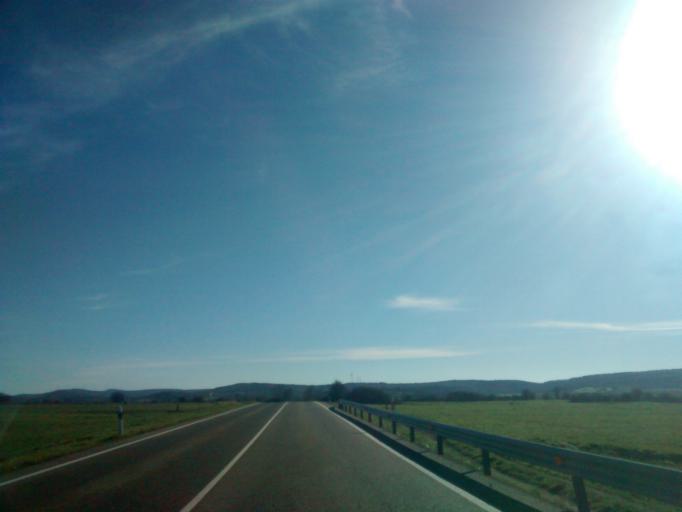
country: ES
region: Cantabria
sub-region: Provincia de Cantabria
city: San Pedro del Romeral
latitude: 42.9788
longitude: -3.8045
